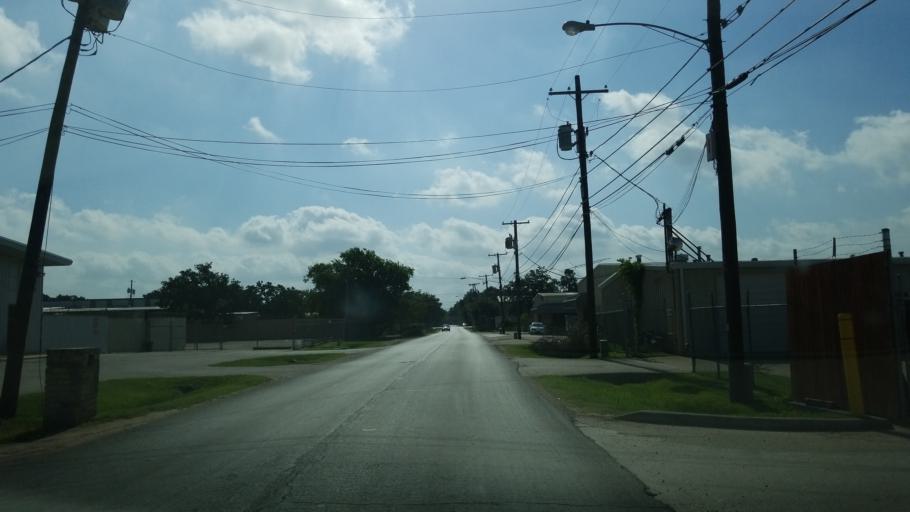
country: US
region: Texas
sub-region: Dallas County
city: Farmers Branch
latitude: 32.8880
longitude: -96.8967
